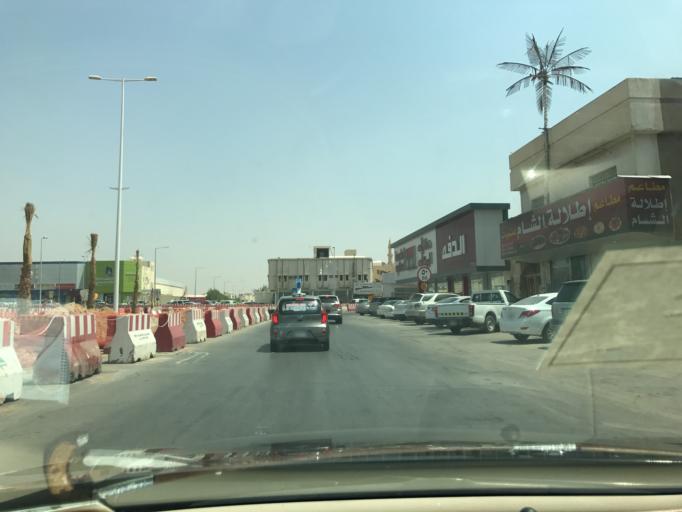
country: SA
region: Ar Riyad
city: Riyadh
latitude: 24.7525
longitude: 46.7692
